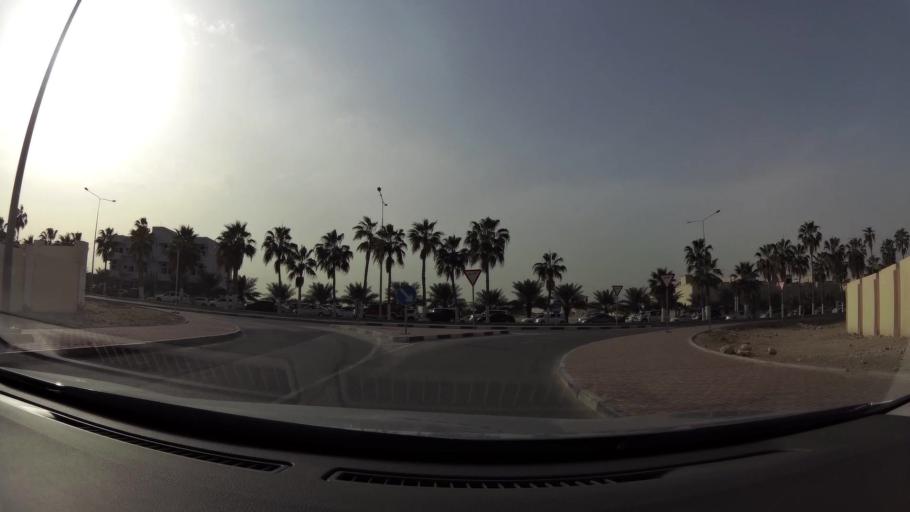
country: QA
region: Baladiyat ad Dawhah
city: Doha
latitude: 25.3198
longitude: 51.4974
